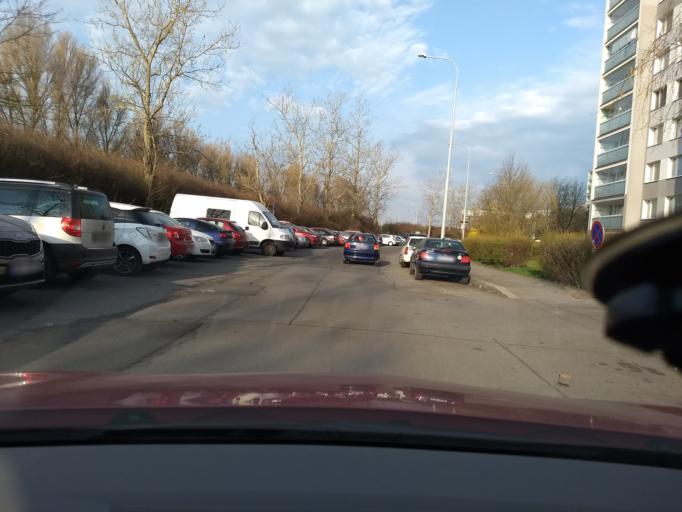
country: CZ
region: Central Bohemia
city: Hostivice
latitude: 50.0449
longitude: 14.3122
